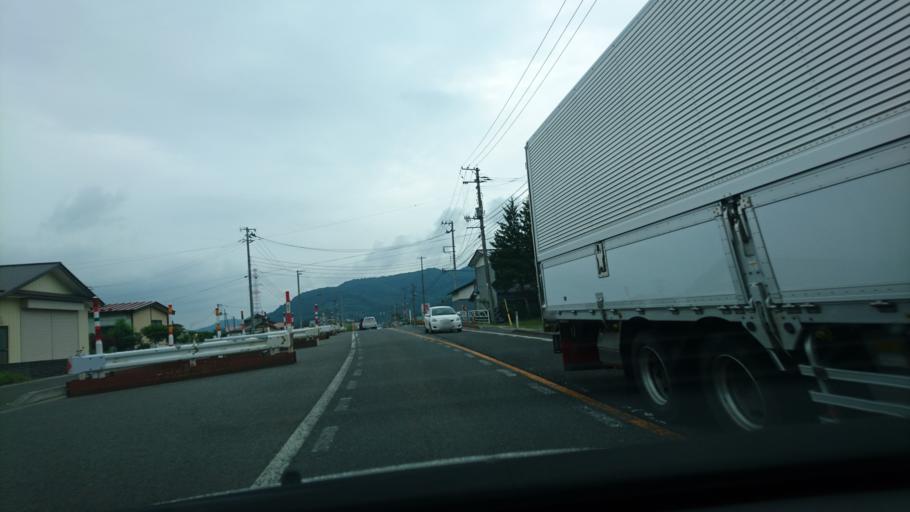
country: JP
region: Miyagi
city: Furukawa
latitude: 38.7360
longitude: 140.7489
